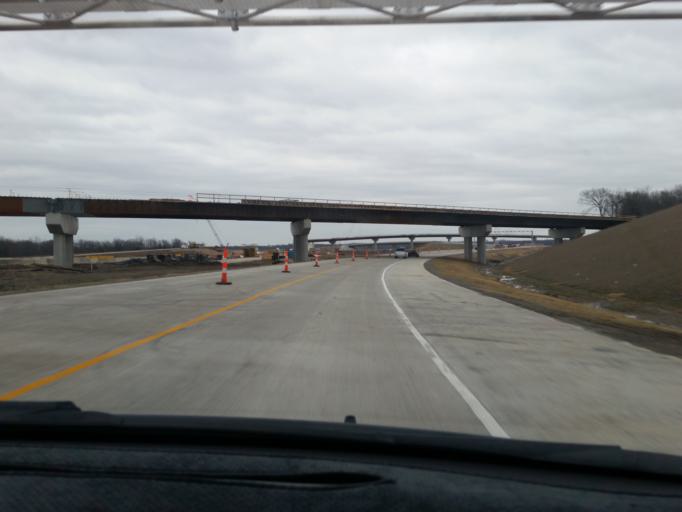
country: US
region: Kansas
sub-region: Douglas County
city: Lawrence
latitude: 38.9401
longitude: -95.1778
